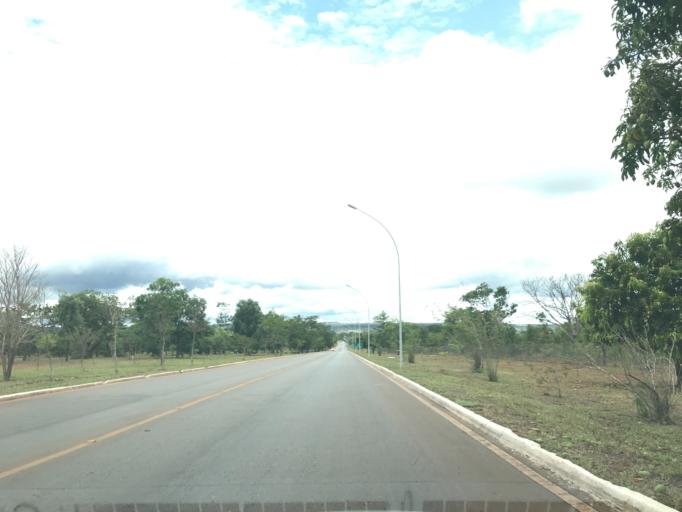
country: BR
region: Federal District
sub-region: Brasilia
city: Brasilia
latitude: -15.7989
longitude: -47.8440
